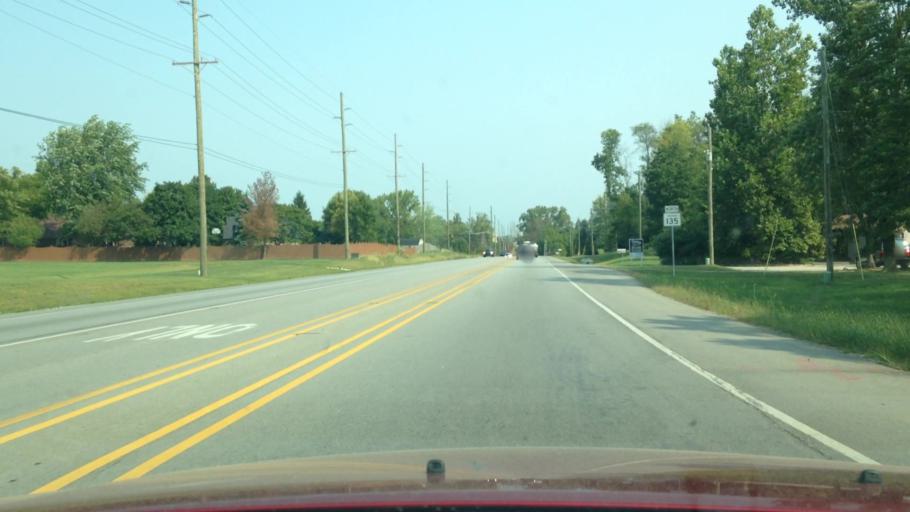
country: US
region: Indiana
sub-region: Johnson County
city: Waterloo
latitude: 39.5632
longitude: -86.1588
